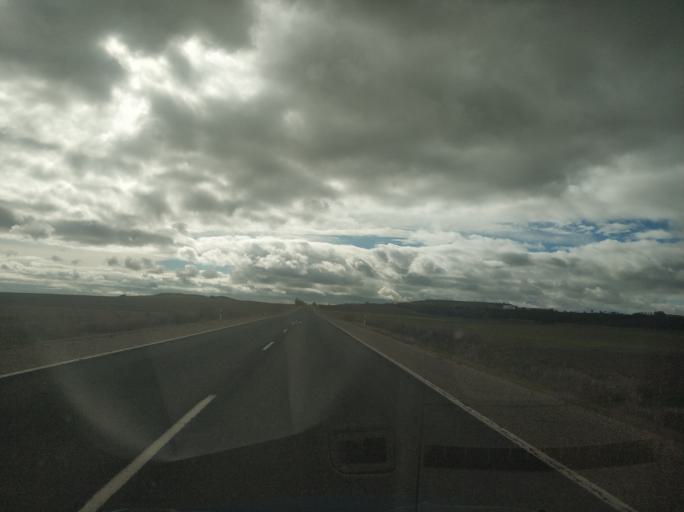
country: ES
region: Castille and Leon
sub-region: Provincia de Zamora
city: Castrillo de la Guarena
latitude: 41.2199
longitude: -5.3167
